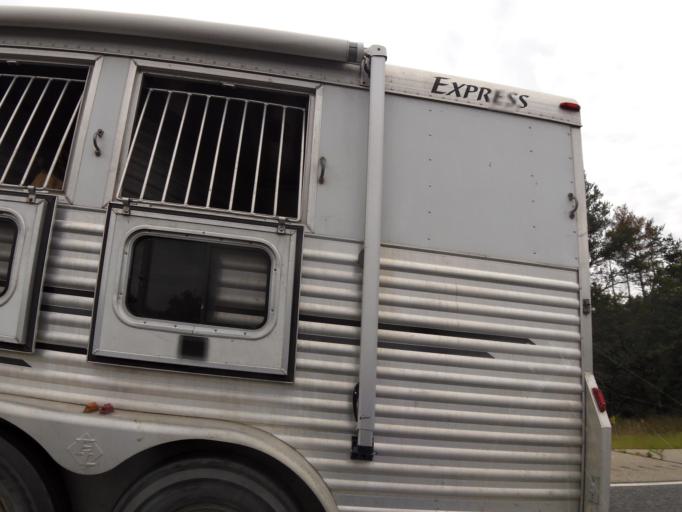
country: US
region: Wisconsin
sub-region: Monroe County
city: Tomah
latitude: 43.9396
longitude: -90.6420
